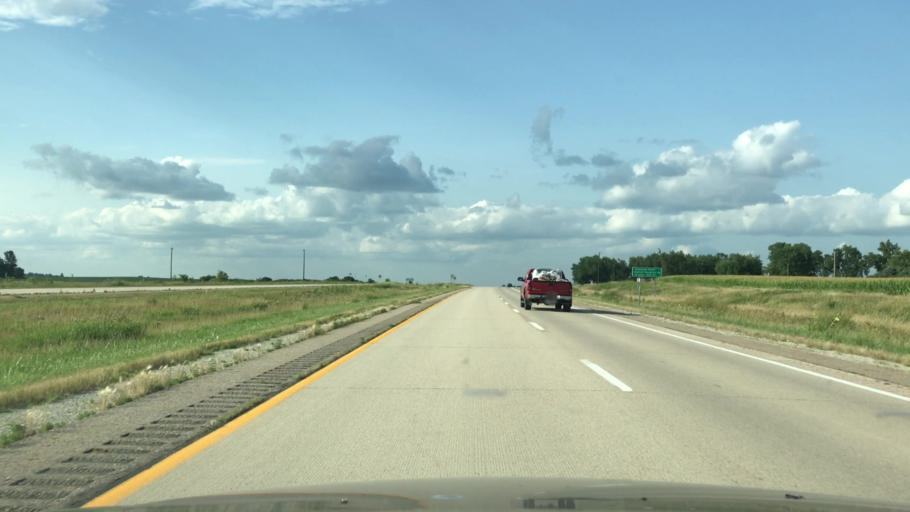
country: US
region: Iowa
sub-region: Osceola County
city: Sibley
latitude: 43.4593
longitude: -95.7127
